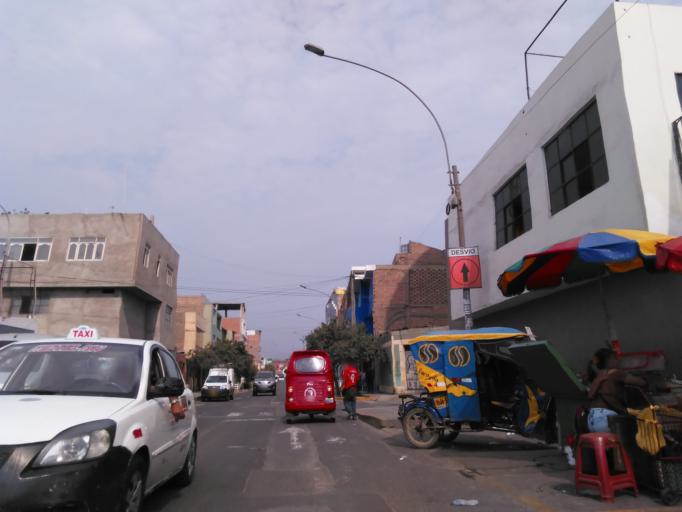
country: PE
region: Callao
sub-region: Callao
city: Callao
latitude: -12.0375
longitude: -77.0797
